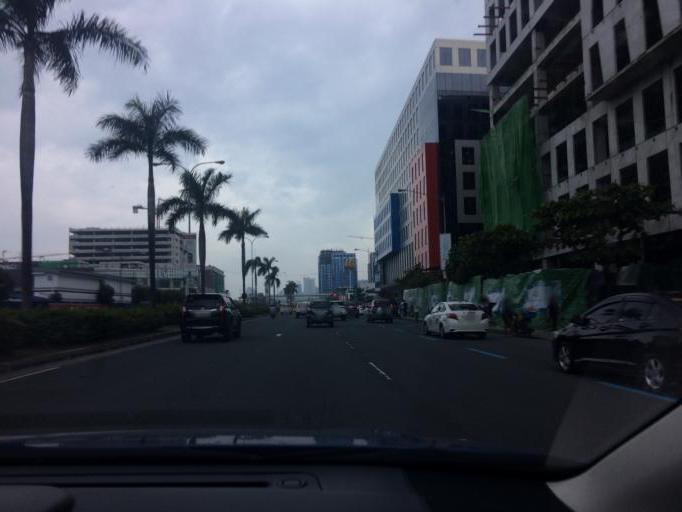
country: PH
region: Metro Manila
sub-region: Makati City
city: Makati City
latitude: 14.5345
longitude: 120.9892
